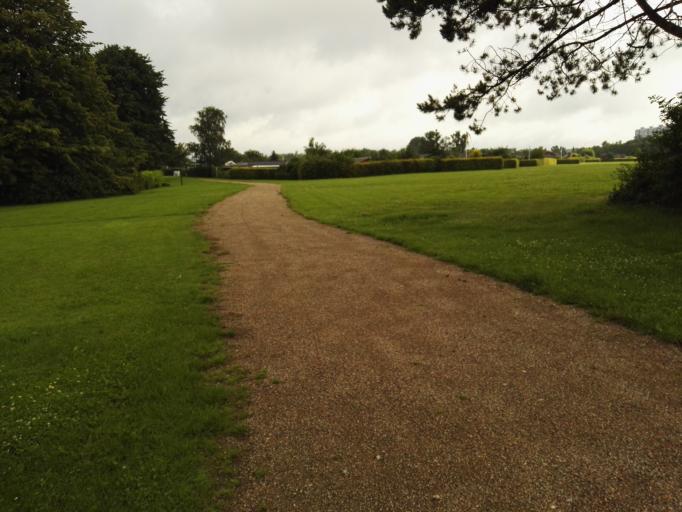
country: DK
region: Capital Region
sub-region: Ballerup Kommune
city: Ballerup
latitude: 55.7117
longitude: 12.3470
